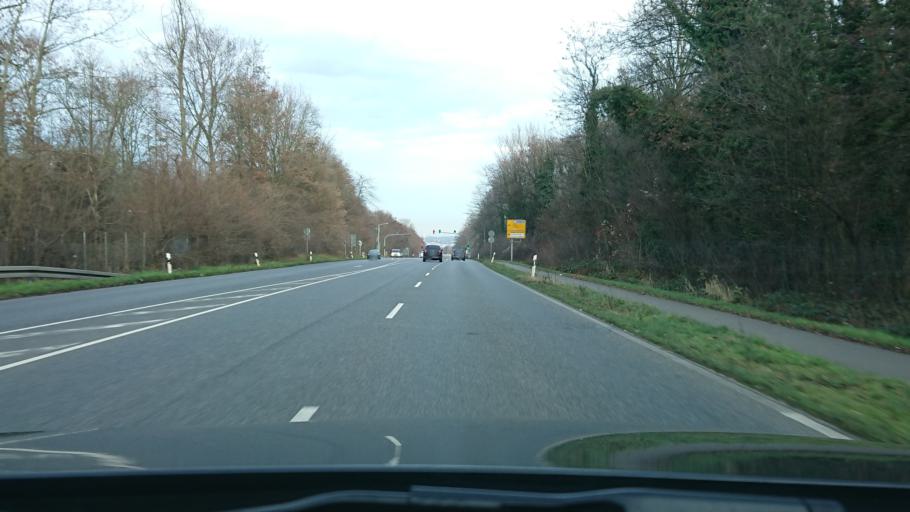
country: DE
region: North Rhine-Westphalia
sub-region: Regierungsbezirk Koln
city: Frechen
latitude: 50.8951
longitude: 6.8058
